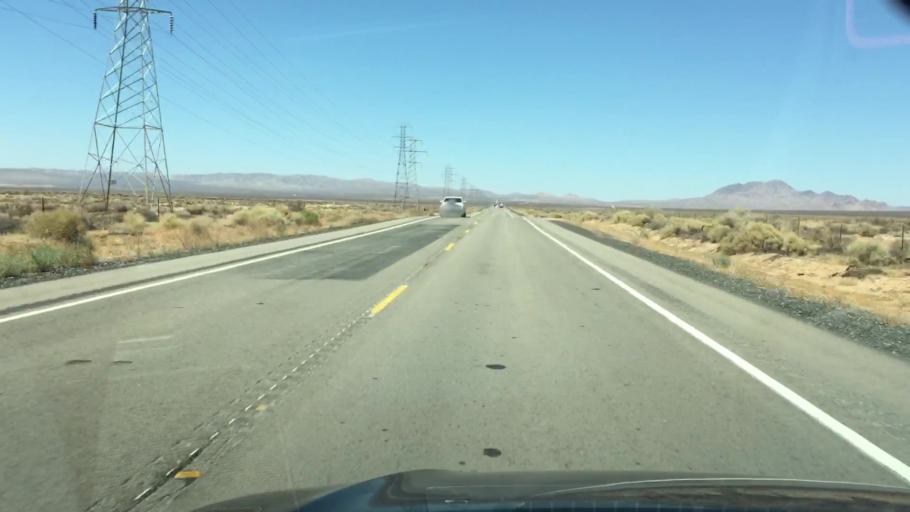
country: US
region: California
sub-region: Kern County
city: Boron
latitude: 35.1831
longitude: -117.5948
